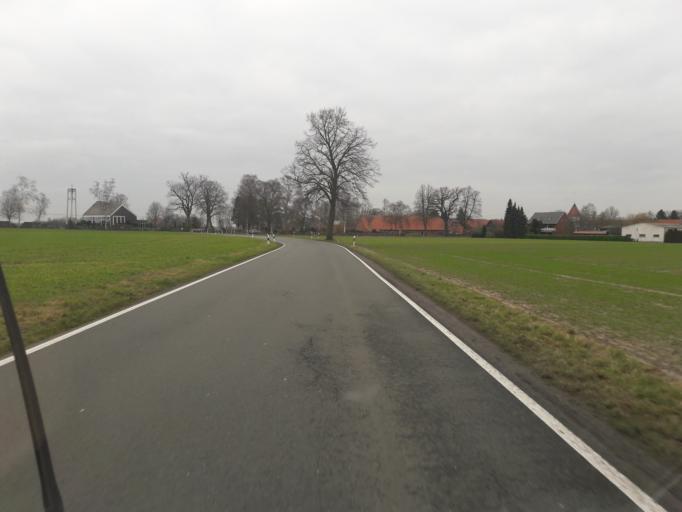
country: DE
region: North Rhine-Westphalia
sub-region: Regierungsbezirk Detmold
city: Hille
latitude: 52.3341
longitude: 8.8337
